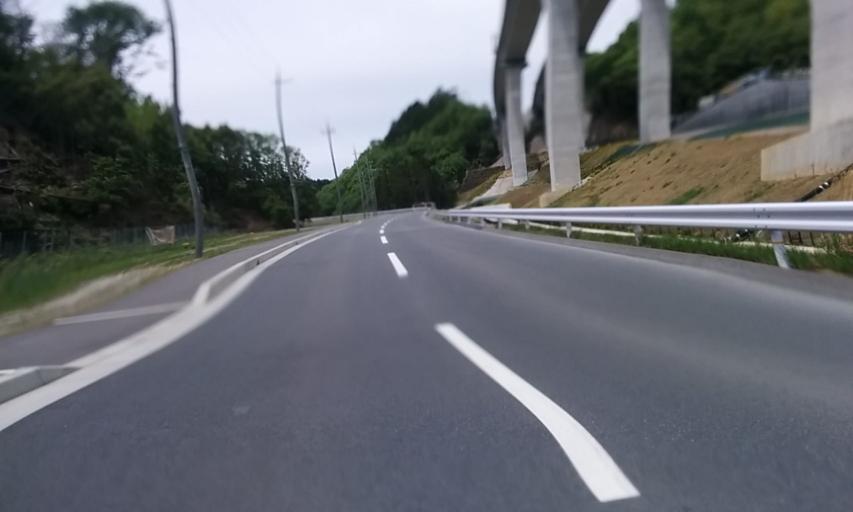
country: JP
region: Osaka
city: Takatsuki
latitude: 34.8886
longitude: 135.6124
